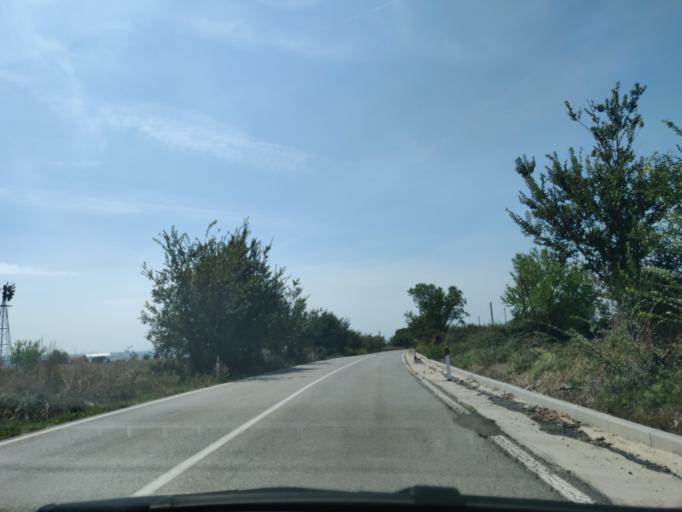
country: IT
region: Latium
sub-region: Provincia di Viterbo
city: Tarquinia
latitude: 42.2278
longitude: 11.7974
